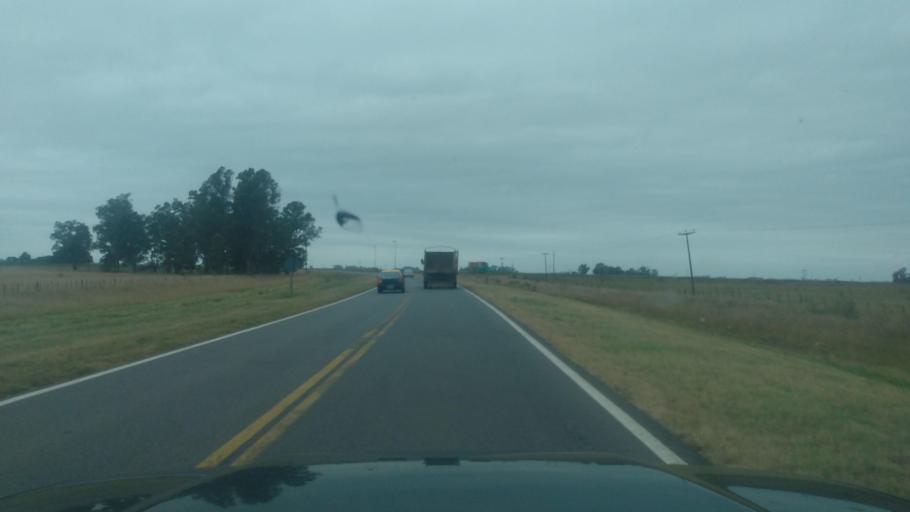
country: AR
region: Buenos Aires
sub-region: Partido de Nueve de Julio
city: Nueve de Julio
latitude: -35.3976
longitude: -60.7484
